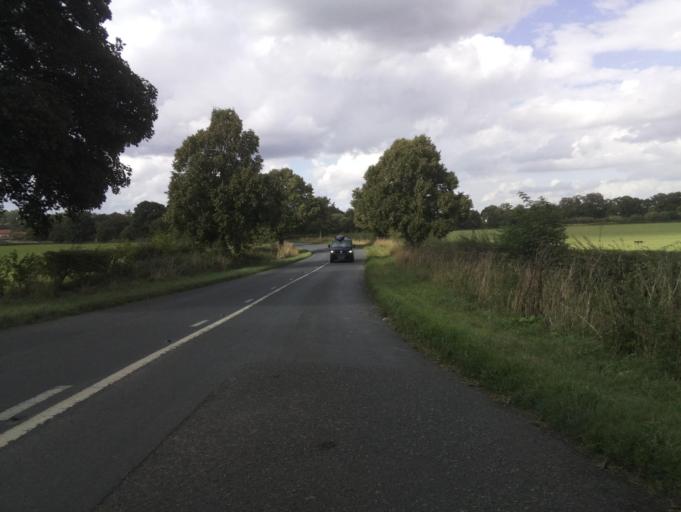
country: GB
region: England
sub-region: North Yorkshire
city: Bedale
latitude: 54.2007
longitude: -1.5832
